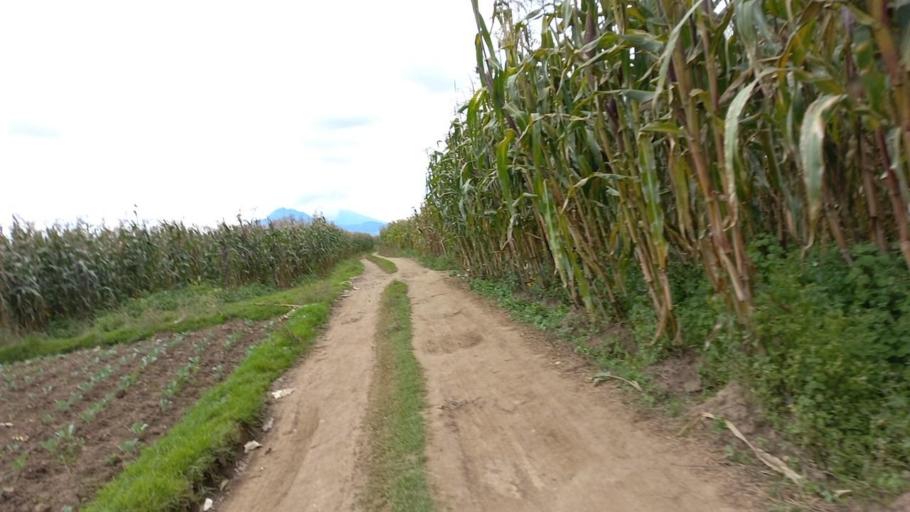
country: GT
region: Totonicapan
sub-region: Municipio de San Andres Xecul
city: San Andres Xecul
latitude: 14.8920
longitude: -91.4669
